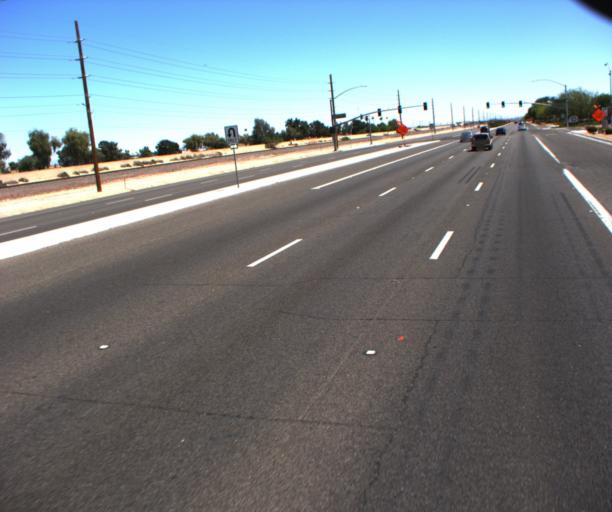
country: US
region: Arizona
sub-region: Maricopa County
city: Sun City West
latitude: 33.6500
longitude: -112.3650
